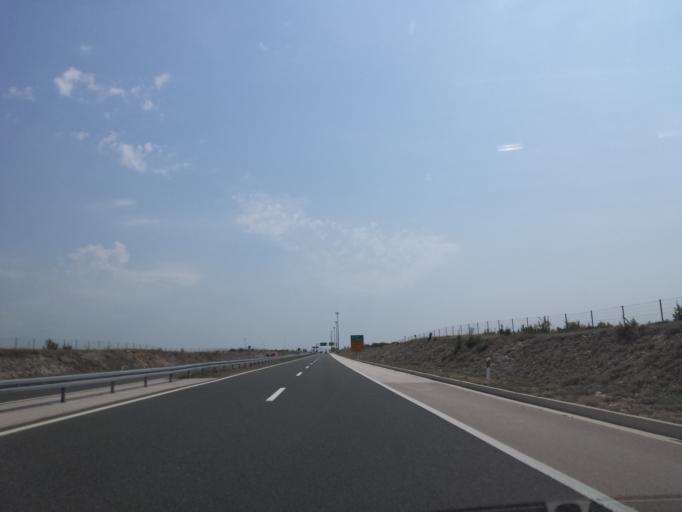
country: HR
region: Sibensko-Kniniska
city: Zaton
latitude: 43.8947
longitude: 15.7836
